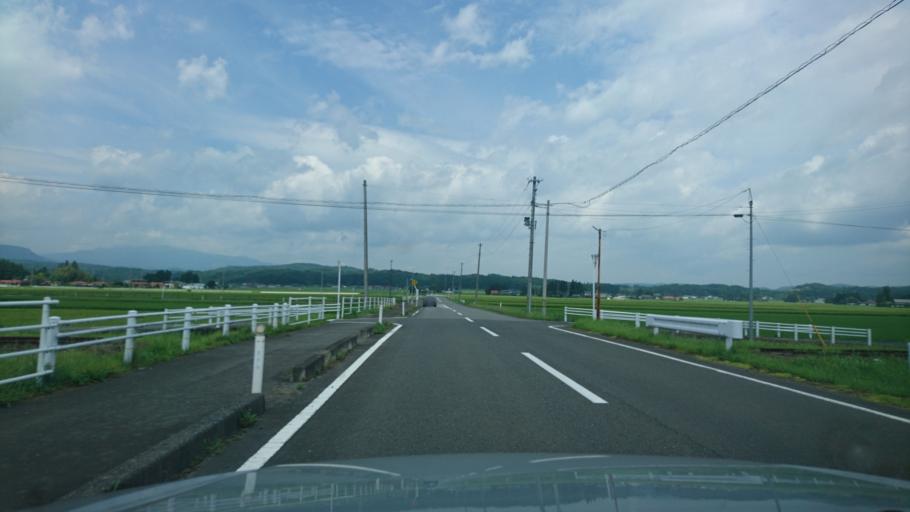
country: JP
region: Iwate
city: Ichinoseki
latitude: 38.8107
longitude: 140.9512
